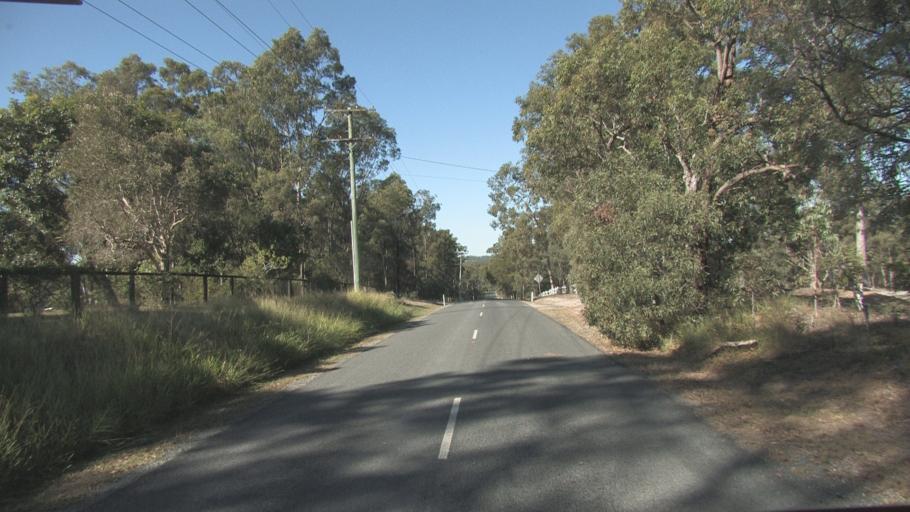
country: AU
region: Queensland
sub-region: Logan
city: Logan Reserve
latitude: -27.7304
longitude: 153.1224
